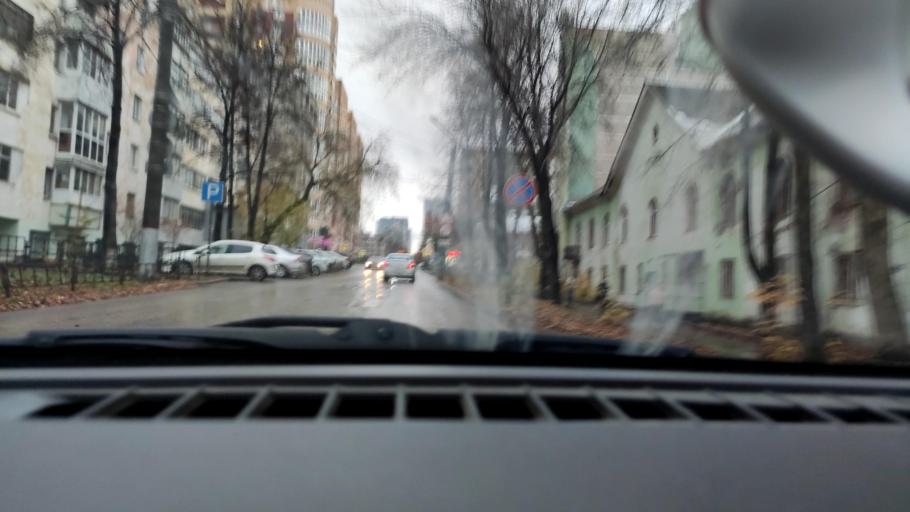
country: RU
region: Perm
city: Perm
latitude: 57.9987
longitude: 56.2380
